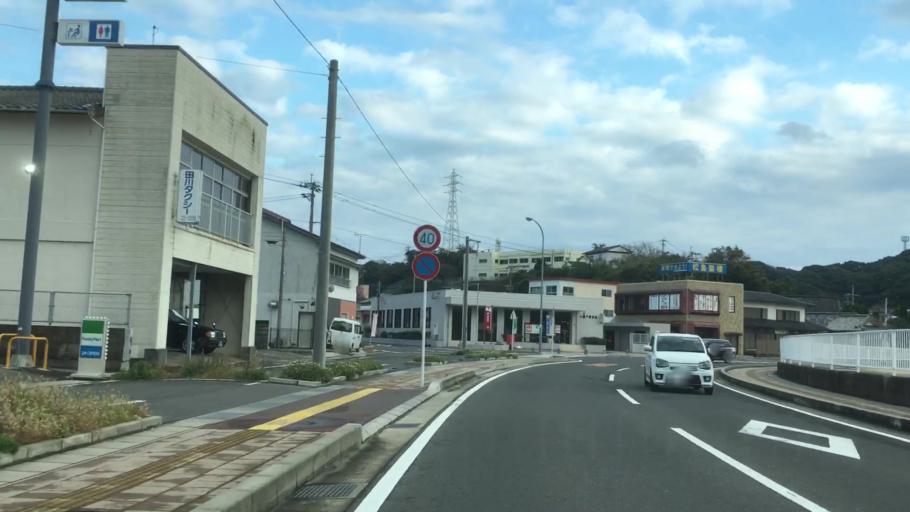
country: JP
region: Nagasaki
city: Togitsu
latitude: 32.9355
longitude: 129.6405
